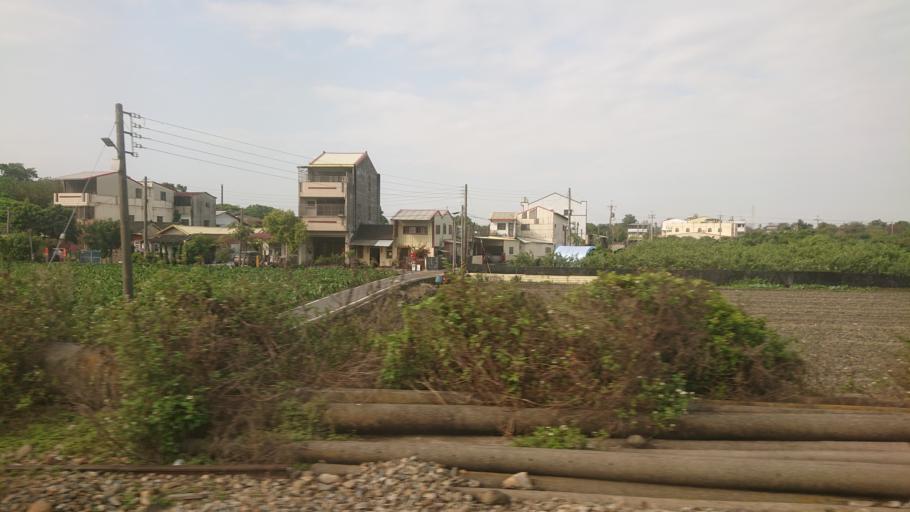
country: TW
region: Taiwan
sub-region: Nantou
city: Nantou
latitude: 23.8983
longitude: 120.5799
